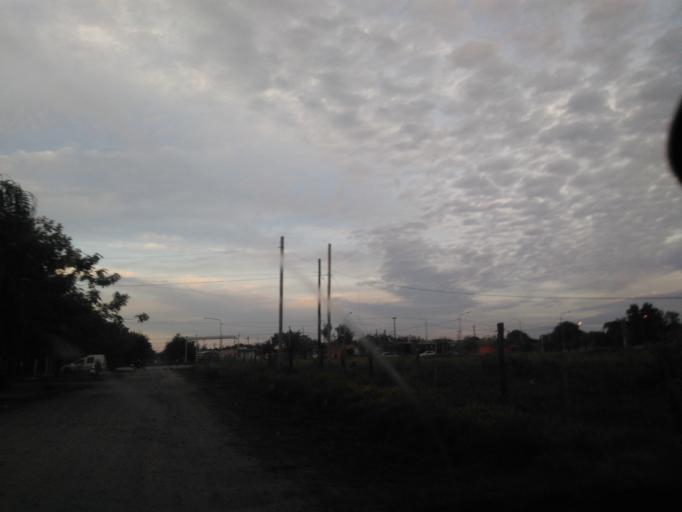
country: AR
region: Chaco
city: Resistencia
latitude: -27.4719
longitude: -58.9850
